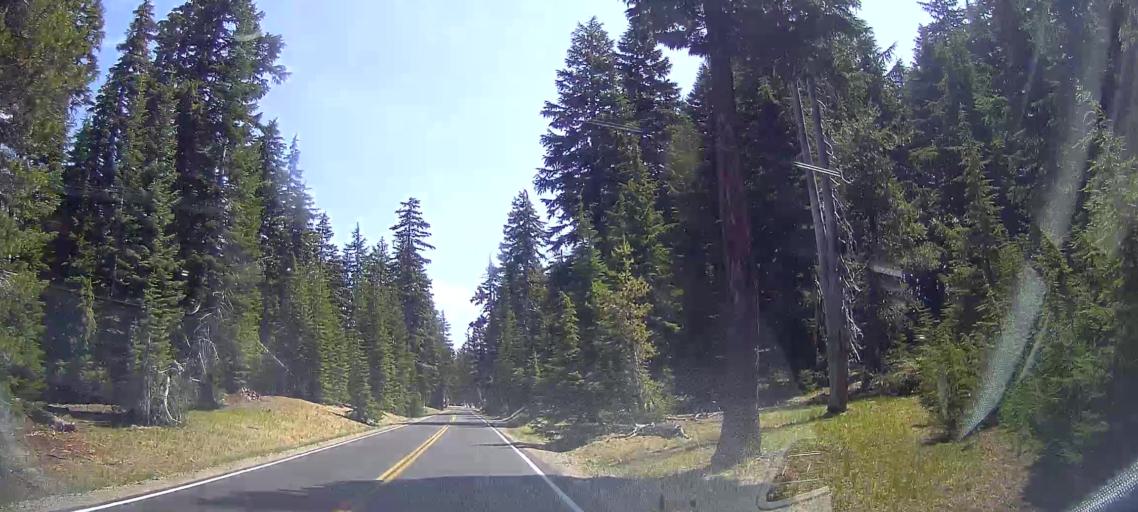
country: US
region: Oregon
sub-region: Jackson County
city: Shady Cove
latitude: 42.9771
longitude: -122.1037
